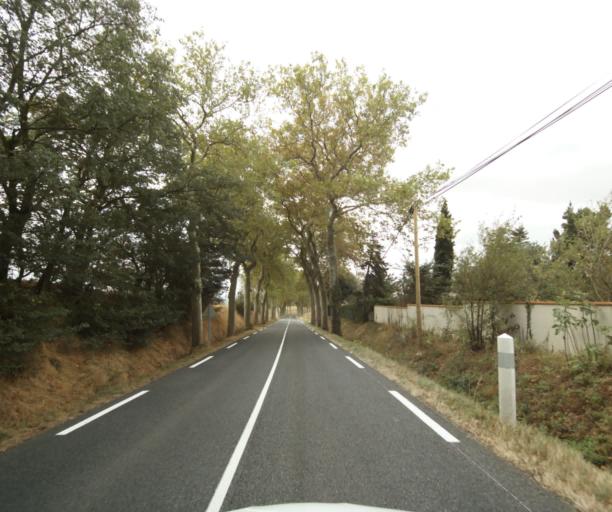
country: FR
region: Midi-Pyrenees
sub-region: Departement de la Haute-Garonne
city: Villefranche-de-Lauragais
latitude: 43.4195
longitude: 1.7184
